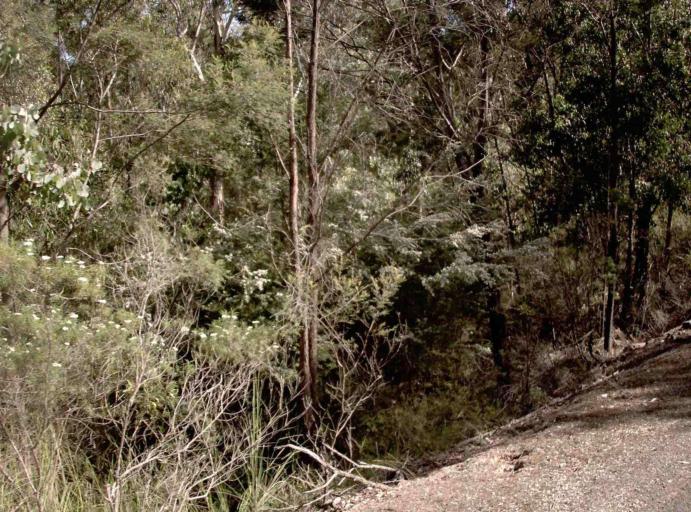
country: AU
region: Victoria
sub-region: East Gippsland
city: Lakes Entrance
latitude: -37.4753
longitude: 148.1252
